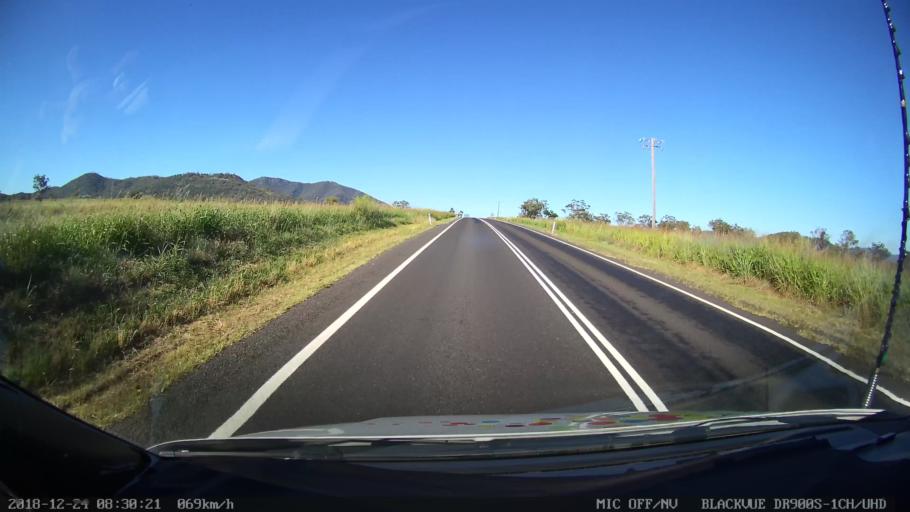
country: AU
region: New South Wales
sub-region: Tamworth Municipality
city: Phillip
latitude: -31.2671
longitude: 150.7254
